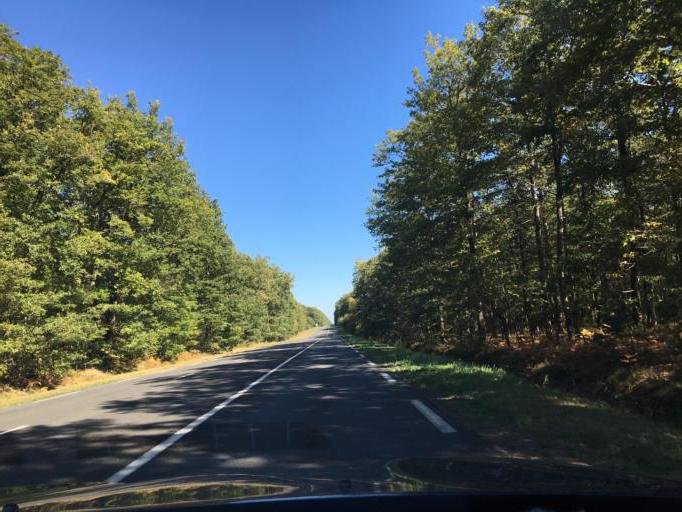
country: FR
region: Centre
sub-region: Departement d'Indre-et-Loire
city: Cheille
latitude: 47.2329
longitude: 0.4055
